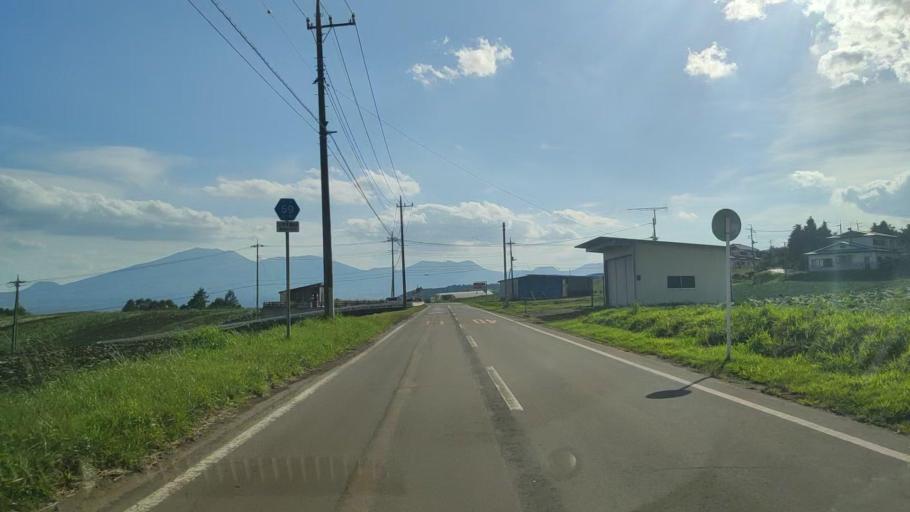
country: JP
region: Nagano
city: Suzaka
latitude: 36.5785
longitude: 138.5645
